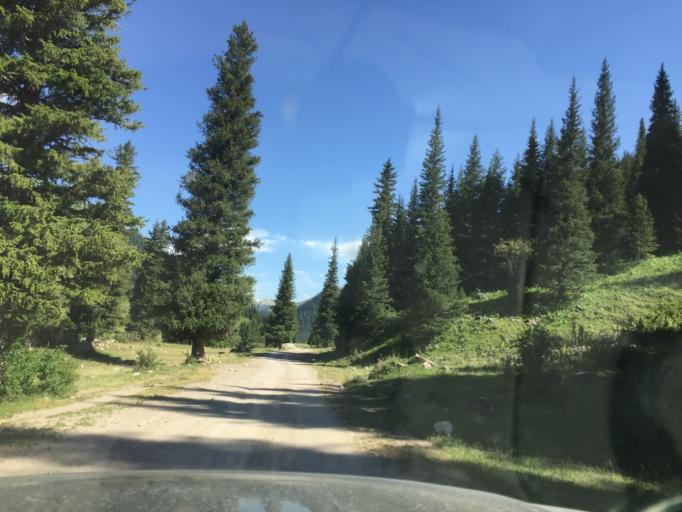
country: KZ
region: Almaty Oblysy
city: Kegen
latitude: 42.6668
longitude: 79.2057
